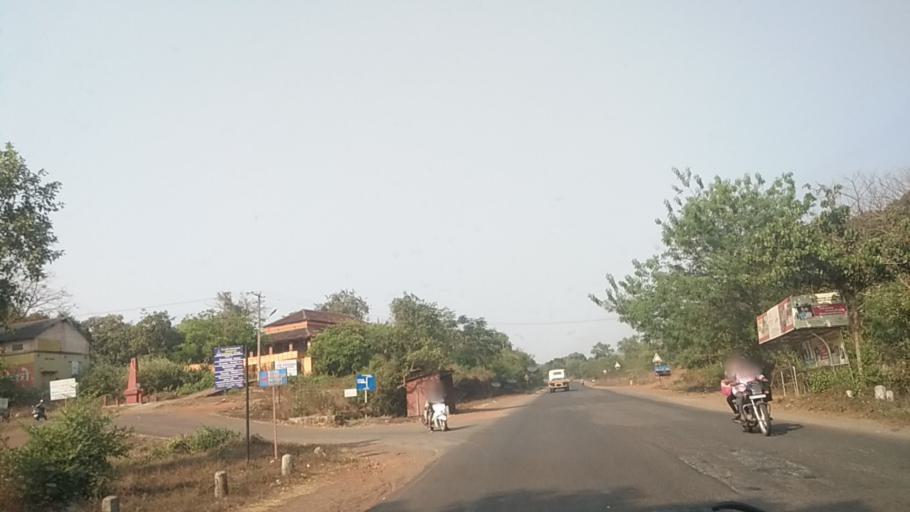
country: IN
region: Goa
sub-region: North Goa
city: Colovale
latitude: 15.6731
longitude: 73.8369
